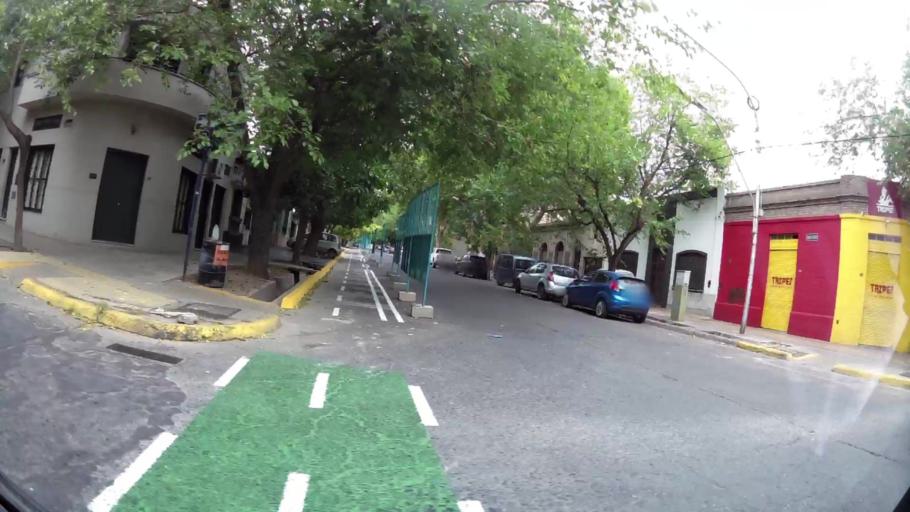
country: AR
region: Mendoza
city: Mendoza
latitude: -32.8850
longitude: -68.8531
